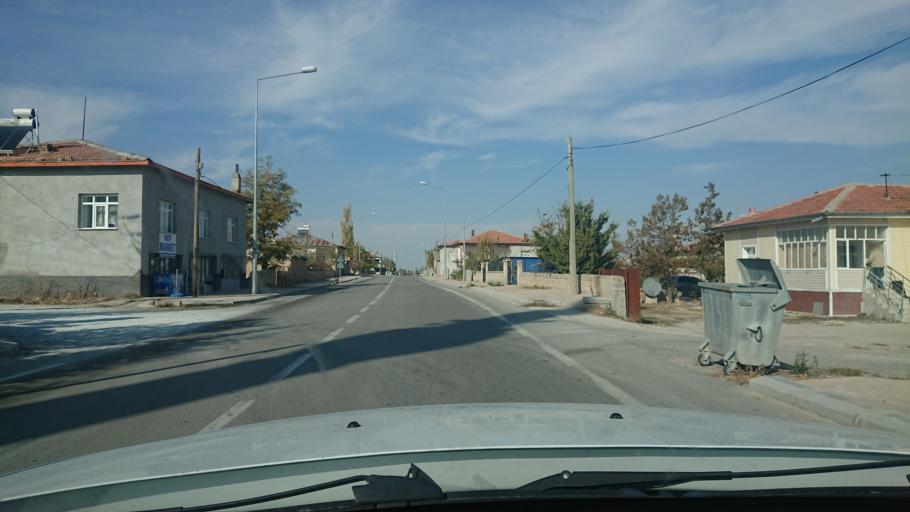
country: TR
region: Aksaray
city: Sultanhani
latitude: 38.2522
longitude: 33.4493
